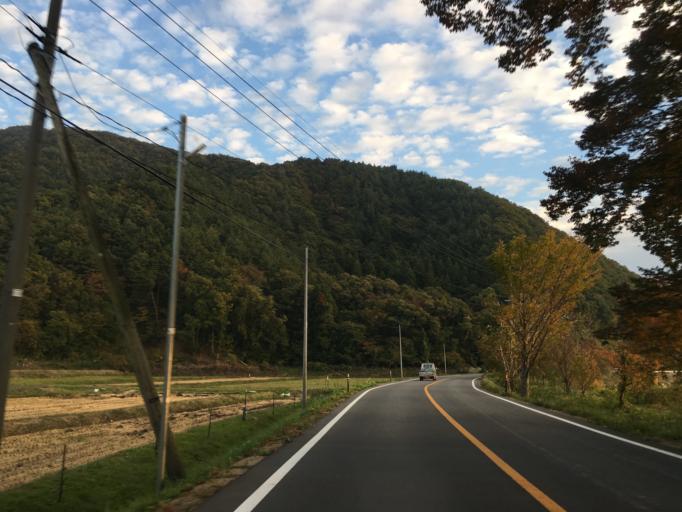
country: JP
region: Fukushima
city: Inawashiro
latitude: 37.4508
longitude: 140.1533
